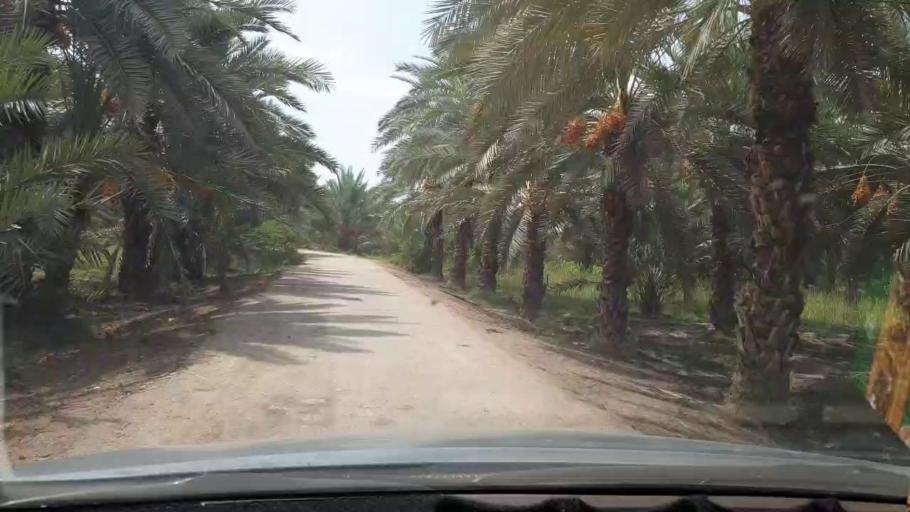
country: PK
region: Sindh
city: Khairpur
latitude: 27.4607
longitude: 68.8216
